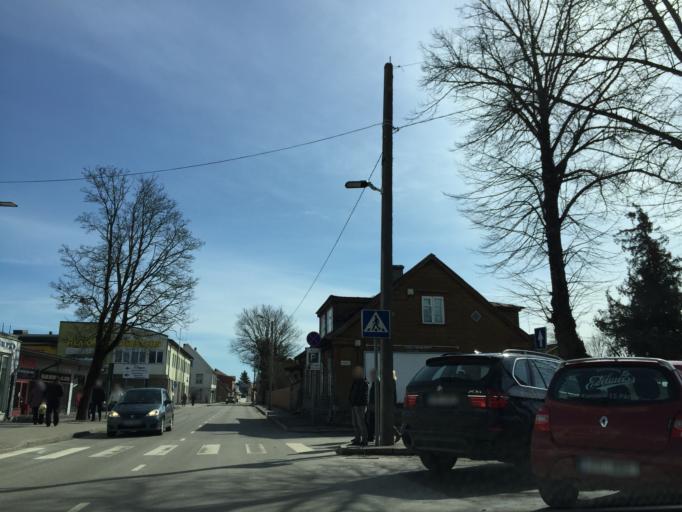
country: EE
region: Paernumaa
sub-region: Paernu linn
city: Parnu
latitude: 58.3821
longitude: 24.5105
